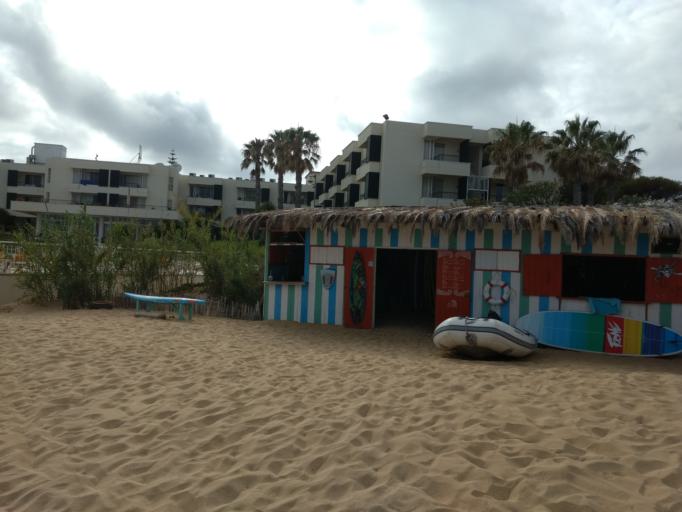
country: PT
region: Madeira
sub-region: Porto Santo
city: Vila de Porto Santo
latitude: 33.0373
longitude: -16.3599
